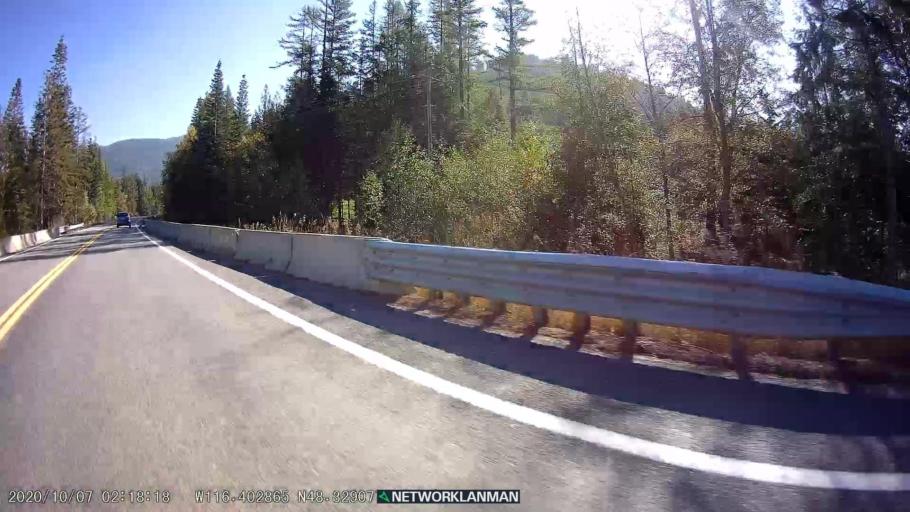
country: US
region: Idaho
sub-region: Bonner County
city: Ponderay
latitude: 48.3291
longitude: -116.4024
